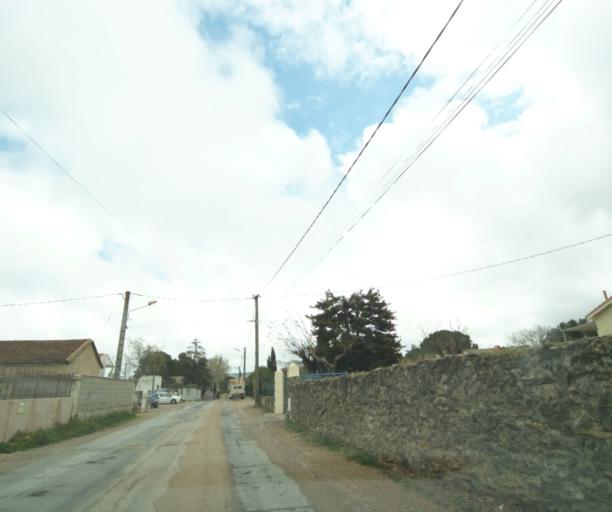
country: FR
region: Languedoc-Roussillon
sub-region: Departement de l'Herault
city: Fabregues
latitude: 43.5536
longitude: 3.7693
